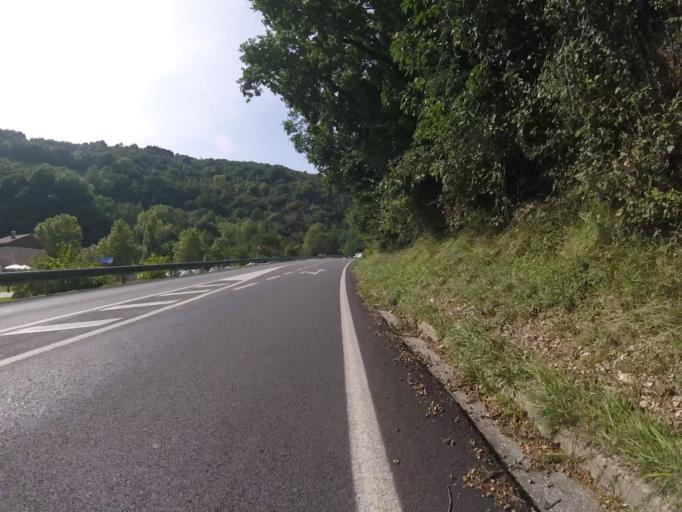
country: ES
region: Navarre
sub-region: Provincia de Navarra
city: Elgorriaga
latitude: 43.1349
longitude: -1.6905
